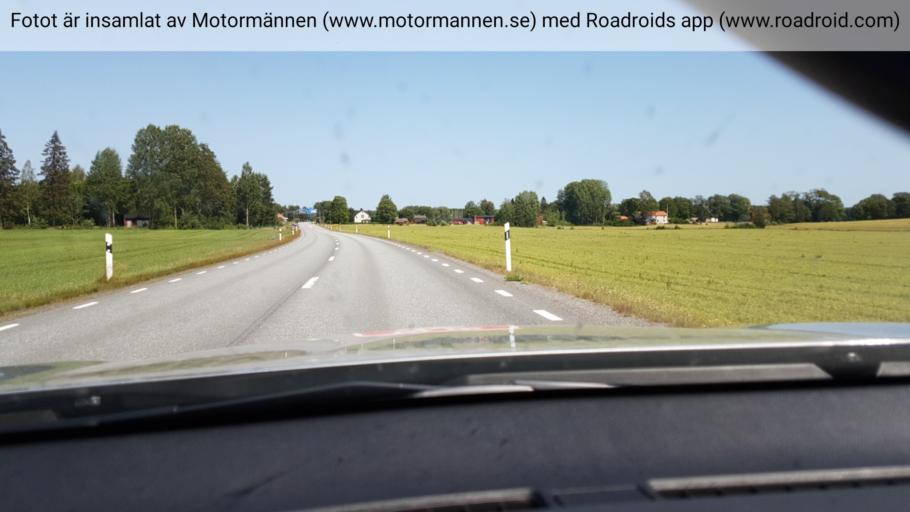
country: SE
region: Joenkoeping
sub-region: Nassjo Kommun
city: Bodafors
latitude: 57.4634
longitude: 14.7540
